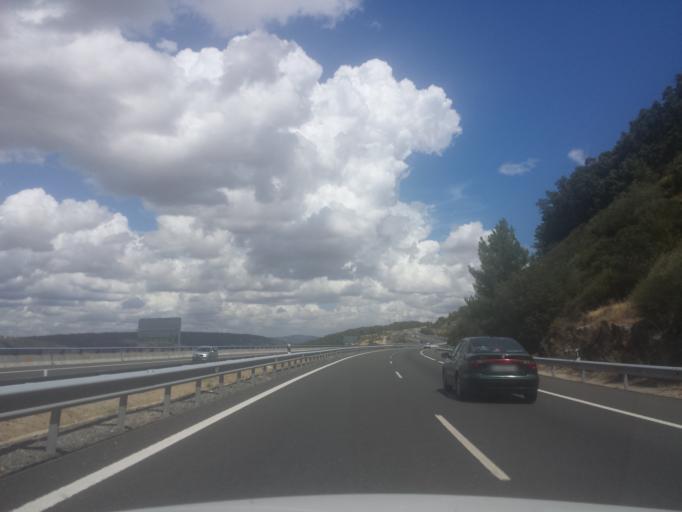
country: ES
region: Castille and Leon
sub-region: Provincia de Salamanca
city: Puerto de Bejar
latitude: 40.3552
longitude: -5.8411
